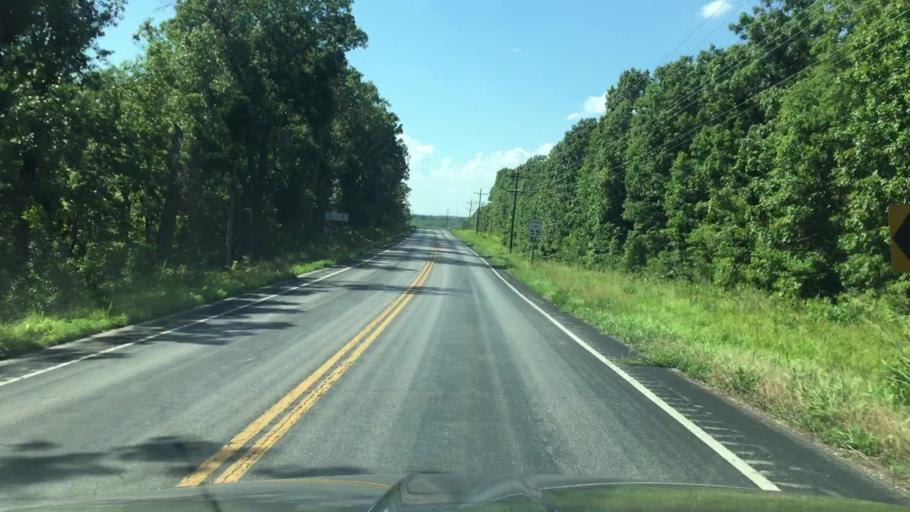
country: US
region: Missouri
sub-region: Camden County
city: Osage Beach
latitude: 38.1312
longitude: -92.5581
